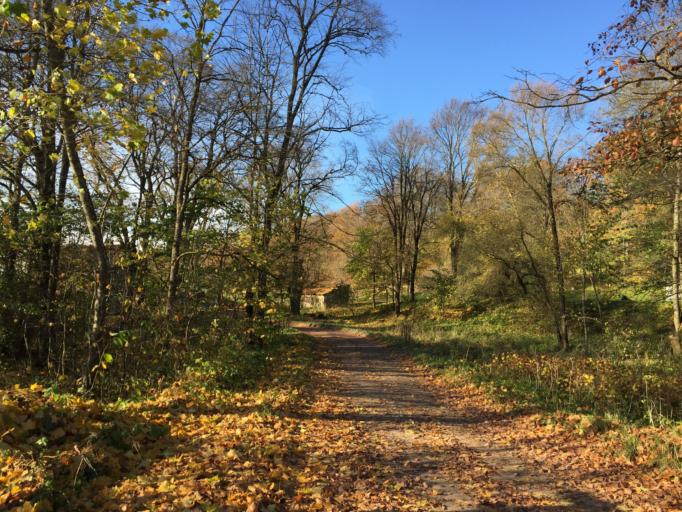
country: LV
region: Skriveri
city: Skriveri
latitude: 56.6146
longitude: 25.1595
